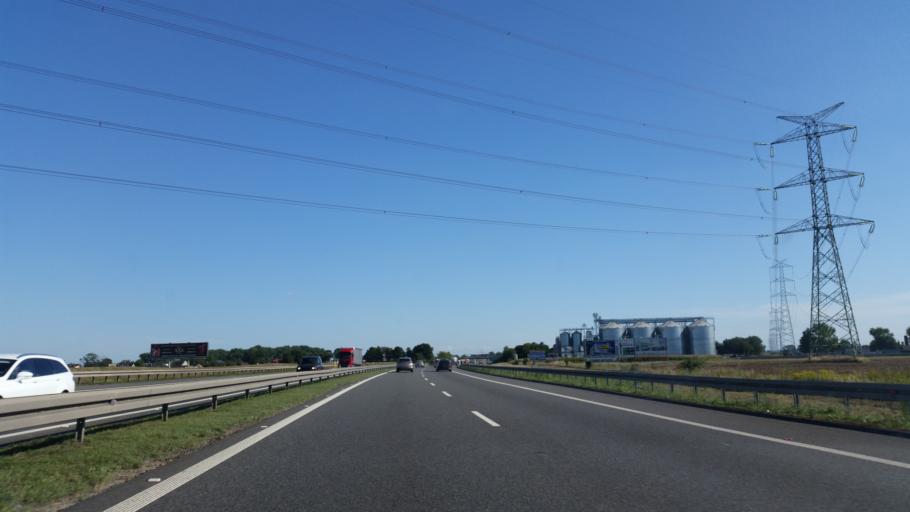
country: PL
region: Lower Silesian Voivodeship
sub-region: Powiat wroclawski
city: Zorawina
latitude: 50.9860
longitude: 17.0577
